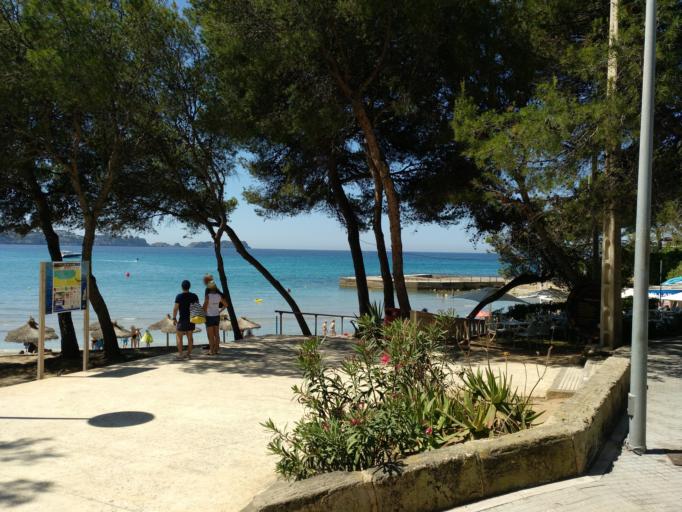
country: ES
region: Balearic Islands
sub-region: Illes Balears
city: Camp de Mar
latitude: 39.5354
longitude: 2.4551
